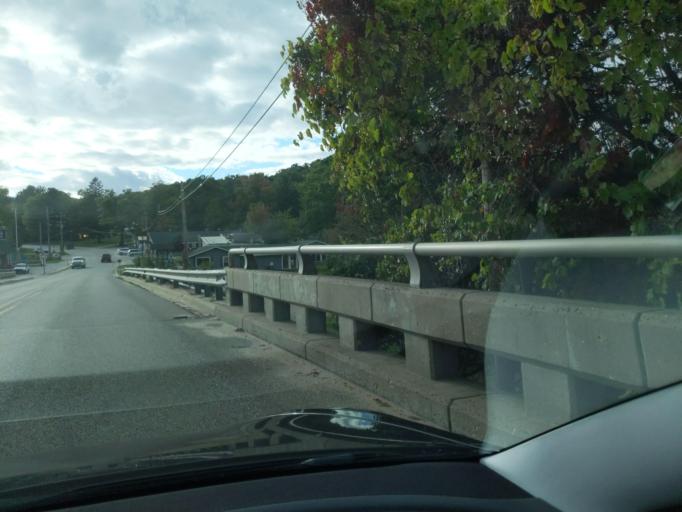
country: US
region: Michigan
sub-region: Kalkaska County
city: Rapid City
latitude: 44.8504
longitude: -85.3277
